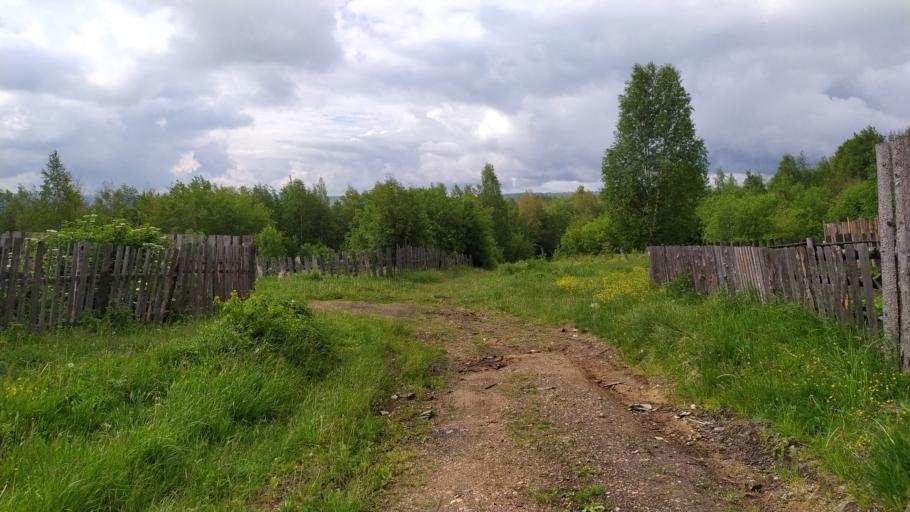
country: RU
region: Perm
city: Gremyachinsk
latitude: 58.5265
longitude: 57.8607
